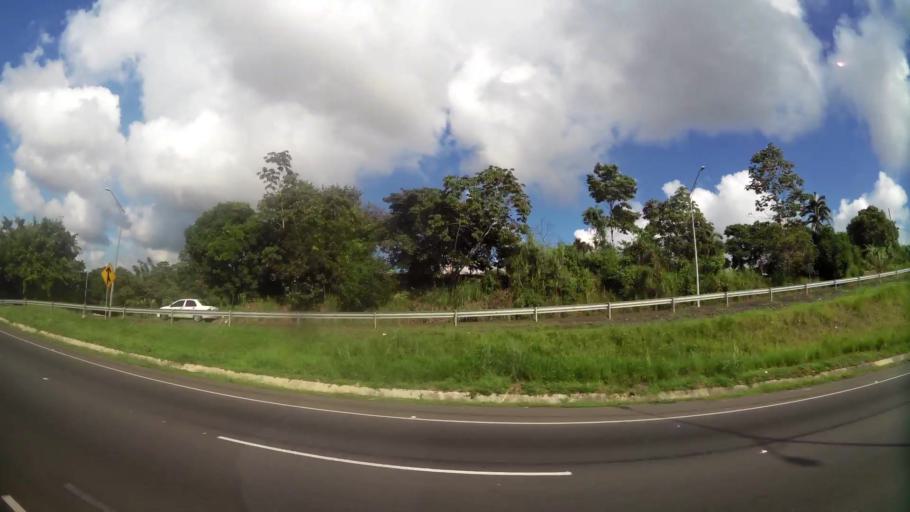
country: PA
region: Panama
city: Vista Alegre
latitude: 8.9312
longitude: -79.6866
